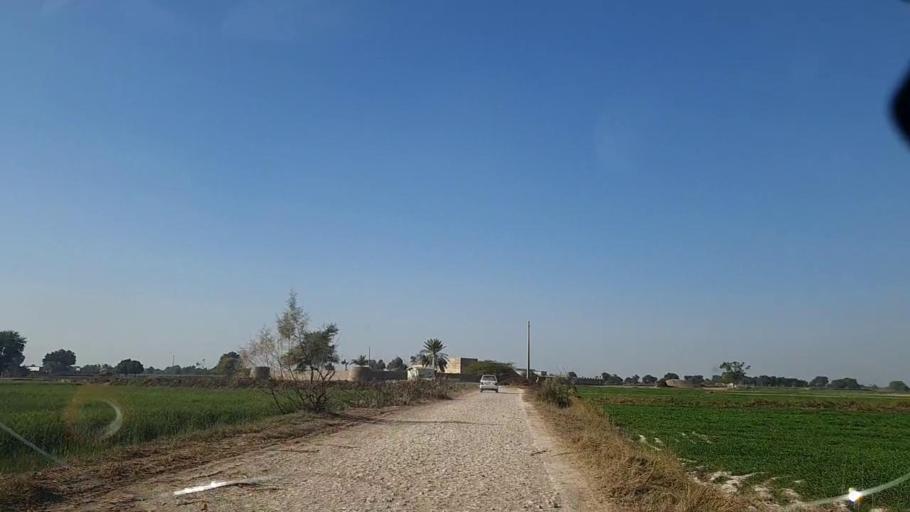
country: PK
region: Sindh
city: Khanpur
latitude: 27.7838
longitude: 69.3538
